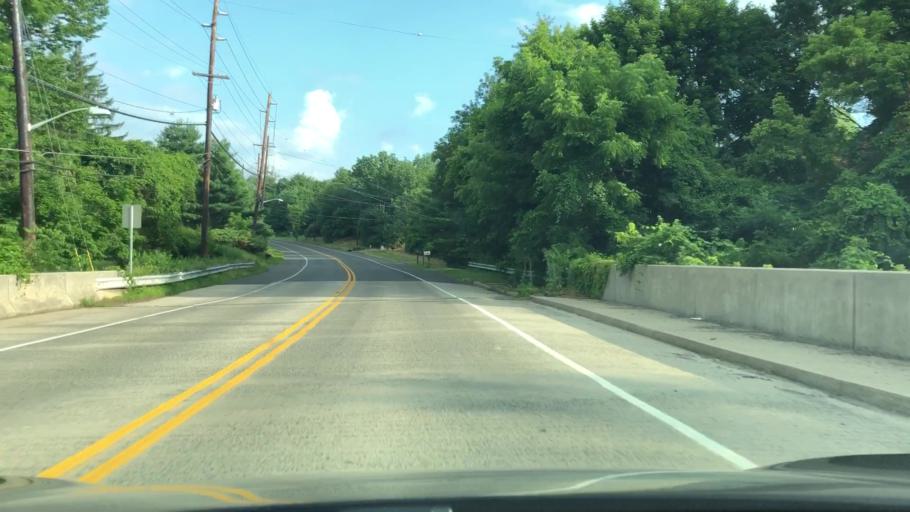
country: US
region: New Jersey
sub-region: Mercer County
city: Lawrenceville
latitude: 40.3432
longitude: -74.7255
